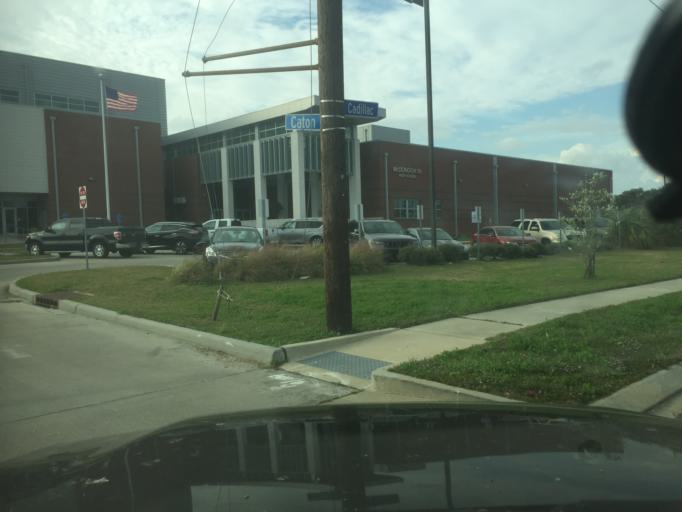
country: US
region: Louisiana
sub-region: Orleans Parish
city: New Orleans
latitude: 29.9976
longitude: -90.0820
